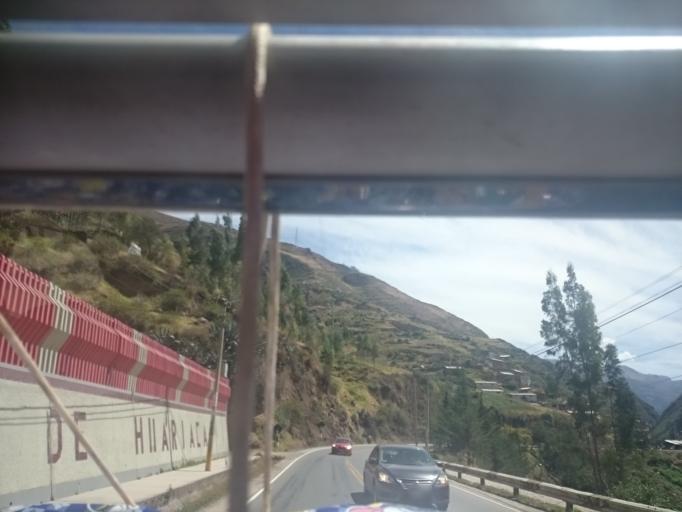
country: PE
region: Pasco
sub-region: Provincia de Pasco
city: Huariaca
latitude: -10.4396
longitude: -76.1902
